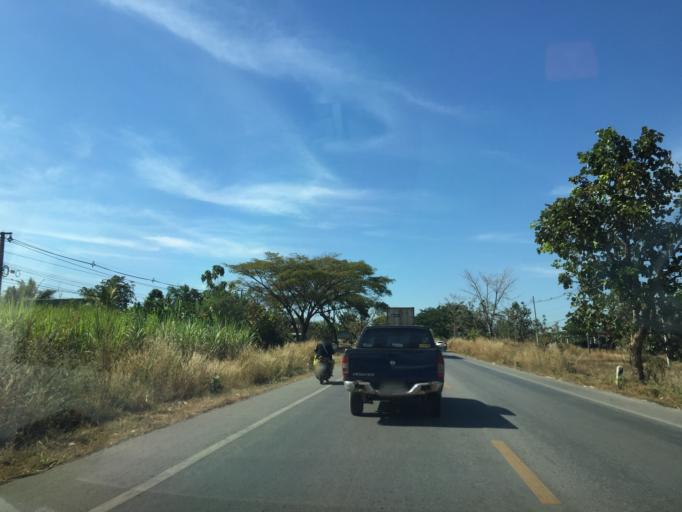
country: TH
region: Changwat Nong Bua Lamphu
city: Na Klang
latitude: 17.3167
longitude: 102.1589
